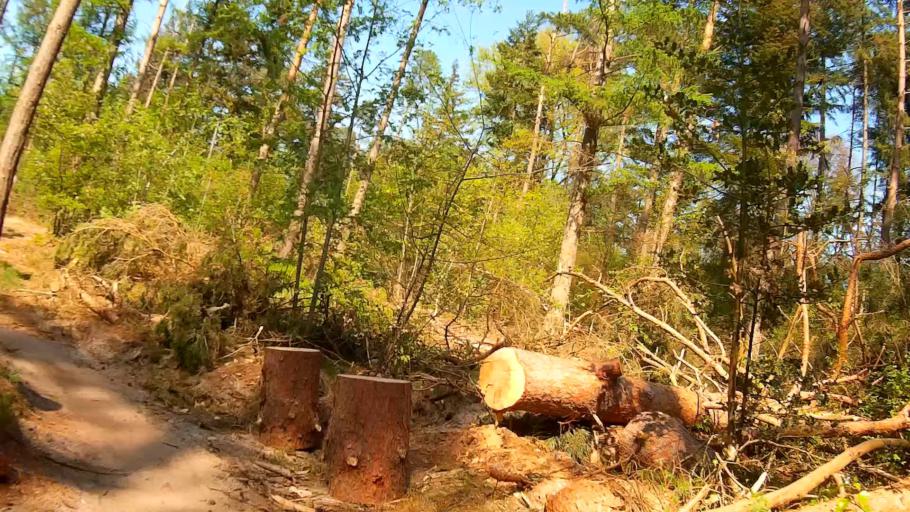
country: NL
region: Utrecht
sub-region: Gemeente Baarn
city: Baarn
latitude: 52.1986
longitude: 5.2710
